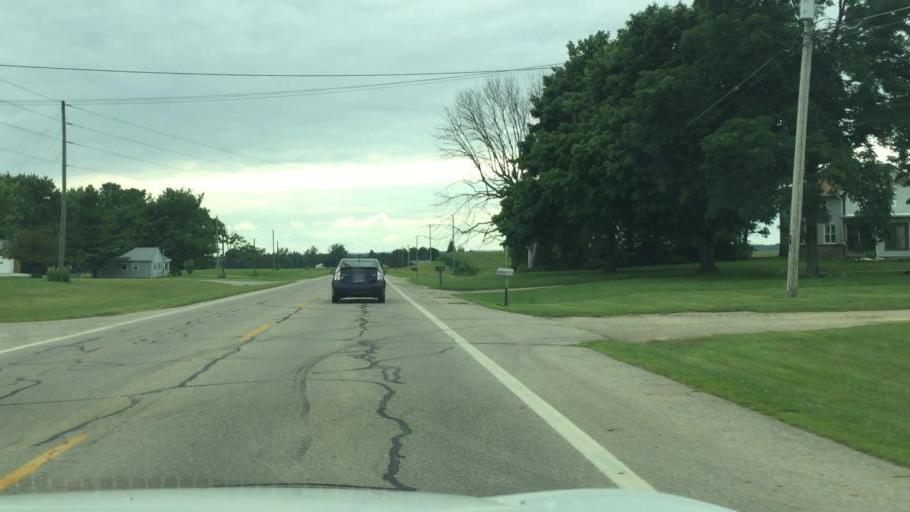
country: US
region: Ohio
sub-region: Champaign County
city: Mechanicsburg
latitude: 40.0784
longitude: -83.6163
